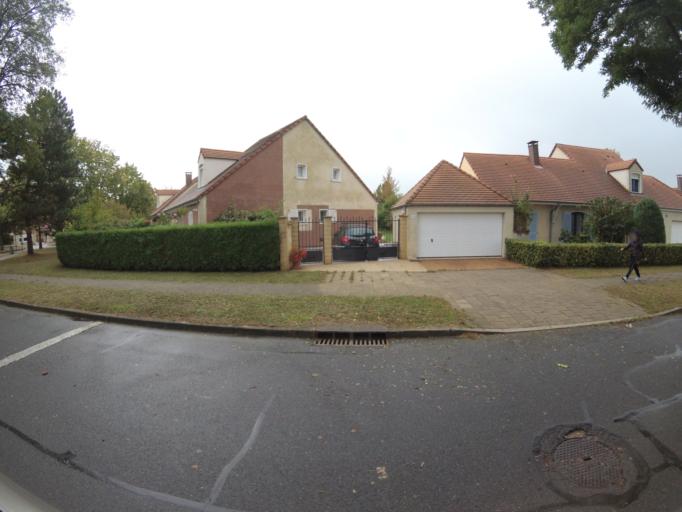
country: FR
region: Ile-de-France
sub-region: Departement de Seine-et-Marne
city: Conches-sur-Gondoire
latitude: 48.8440
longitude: 2.7195
